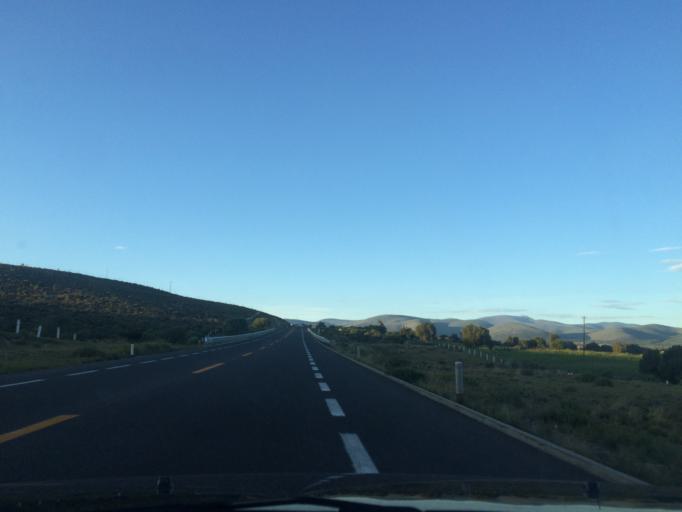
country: MX
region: Puebla
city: Cuacnopalan
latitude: 18.7929
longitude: -97.4892
